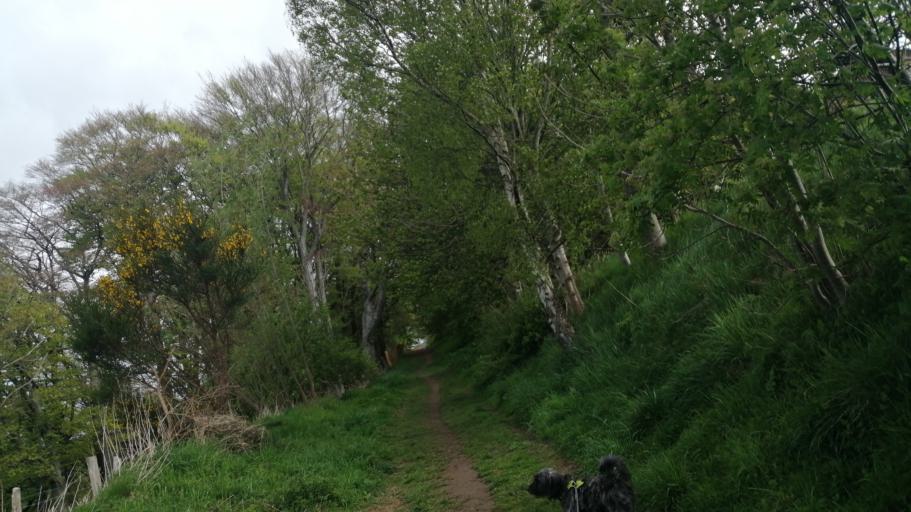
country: GB
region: Scotland
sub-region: Moray
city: Keith
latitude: 57.5363
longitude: -2.9599
